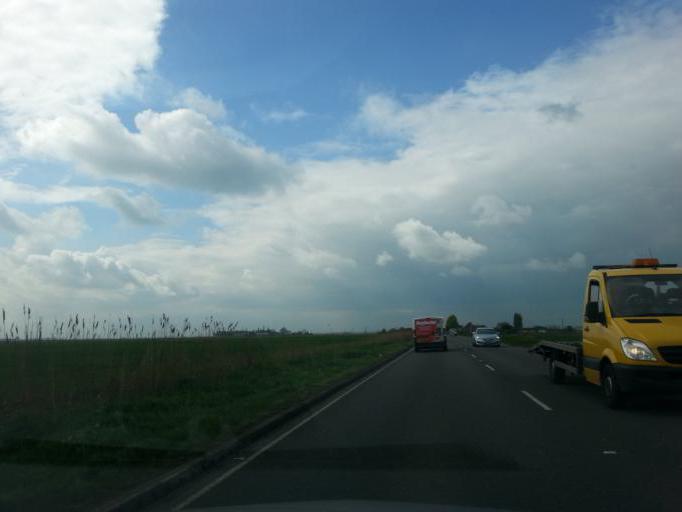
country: GB
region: England
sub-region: Peterborough
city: Thorney
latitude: 52.6153
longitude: -0.0067
